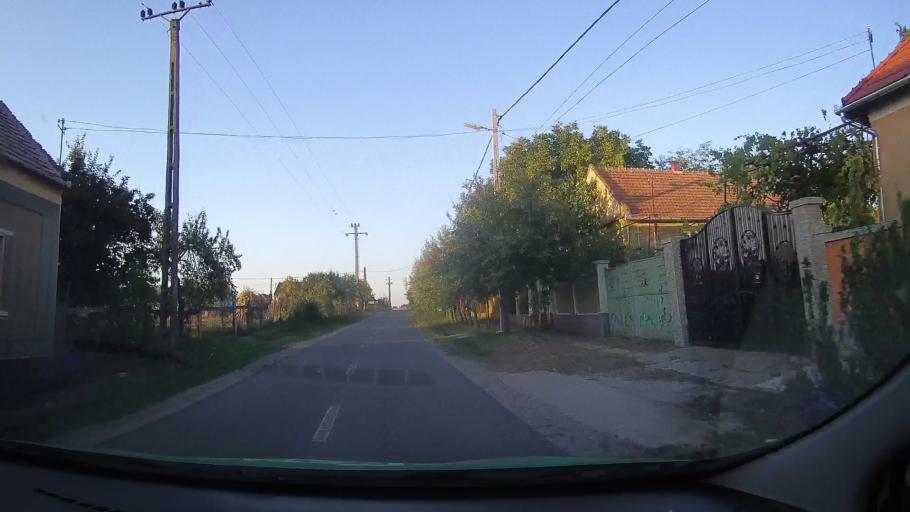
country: RO
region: Bihor
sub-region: Comuna Rosiori
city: Rosiori
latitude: 47.2542
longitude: 21.9900
